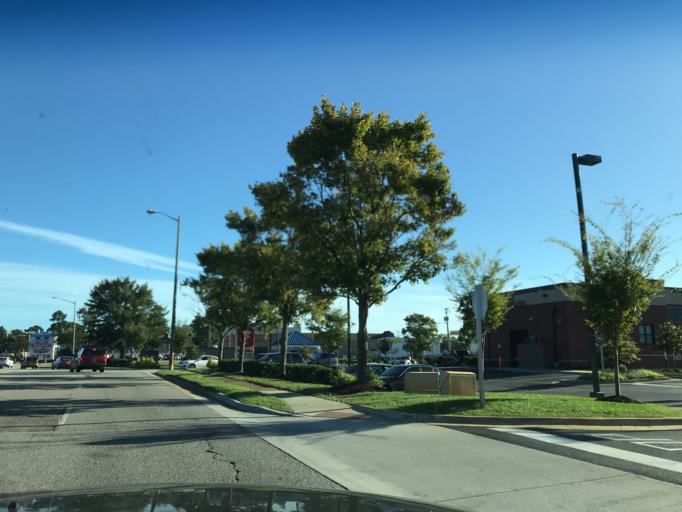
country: US
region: Virginia
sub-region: City of Chesapeake
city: Chesapeake
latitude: 36.7700
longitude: -76.2511
